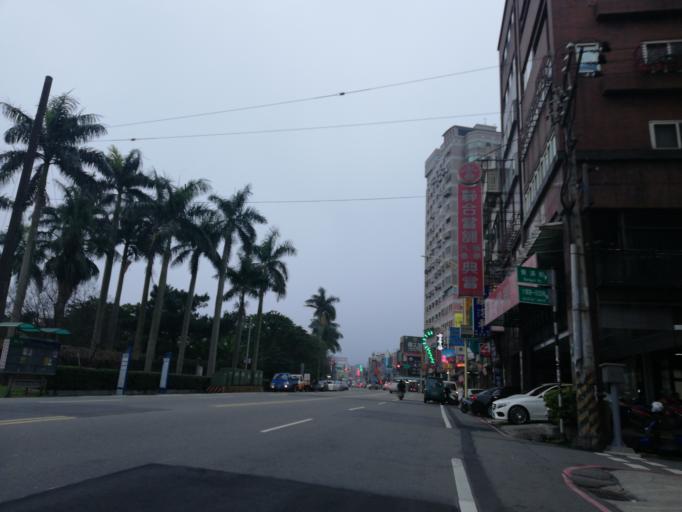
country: TW
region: Taiwan
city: Taoyuan City
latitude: 24.9720
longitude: 121.3018
